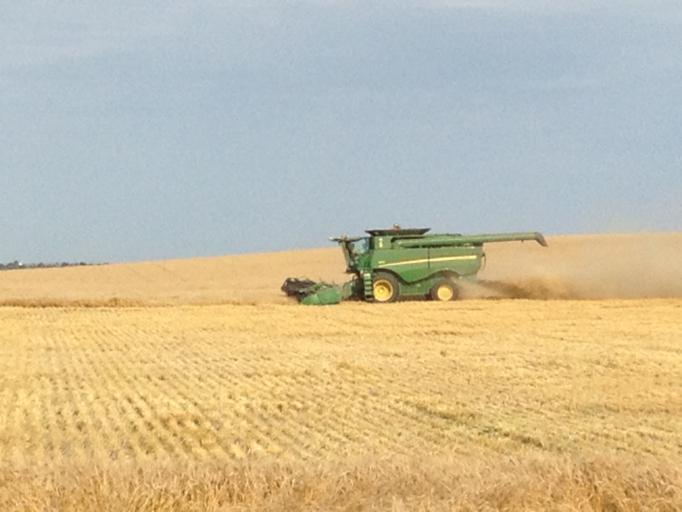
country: US
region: North Dakota
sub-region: Hettinger County
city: Mott
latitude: 46.4152
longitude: -102.6340
